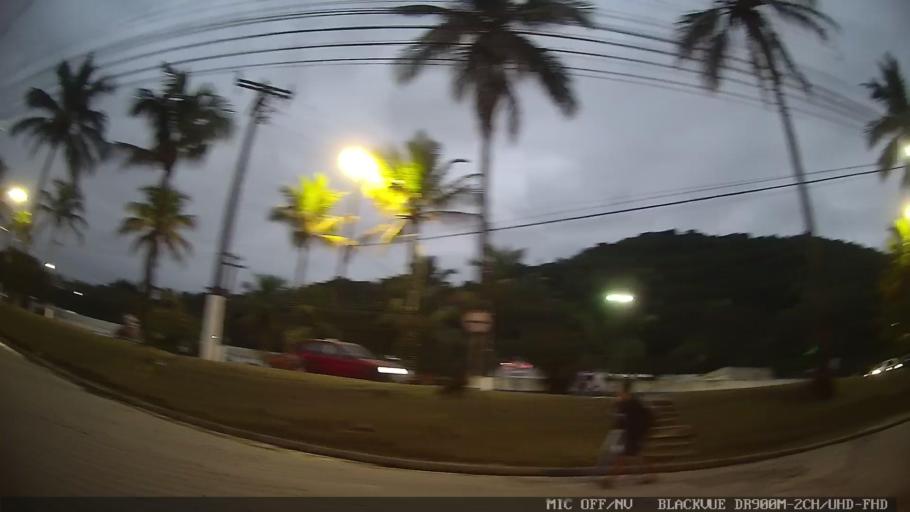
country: BR
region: Sao Paulo
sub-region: Guaruja
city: Guaruja
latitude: -23.9888
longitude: -46.2622
